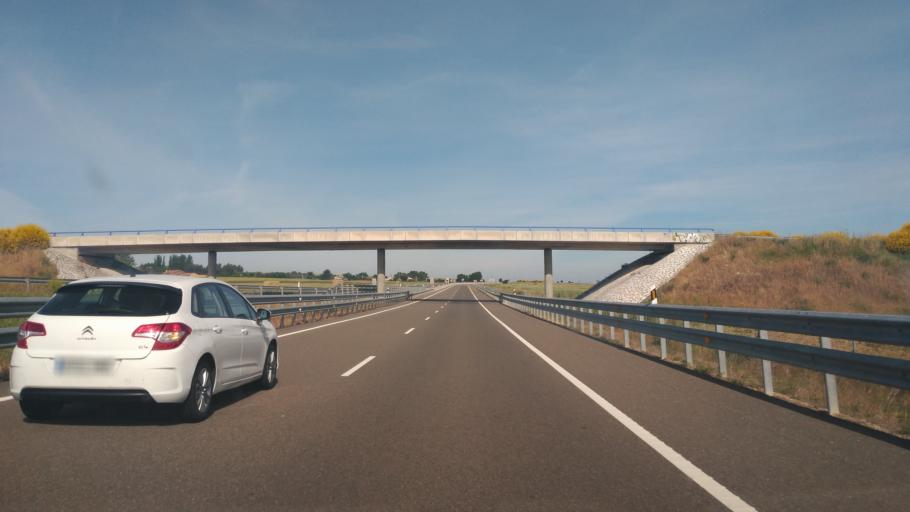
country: ES
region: Castille and Leon
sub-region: Provincia de Zamora
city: Morales del Vino
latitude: 41.4560
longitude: -5.7233
